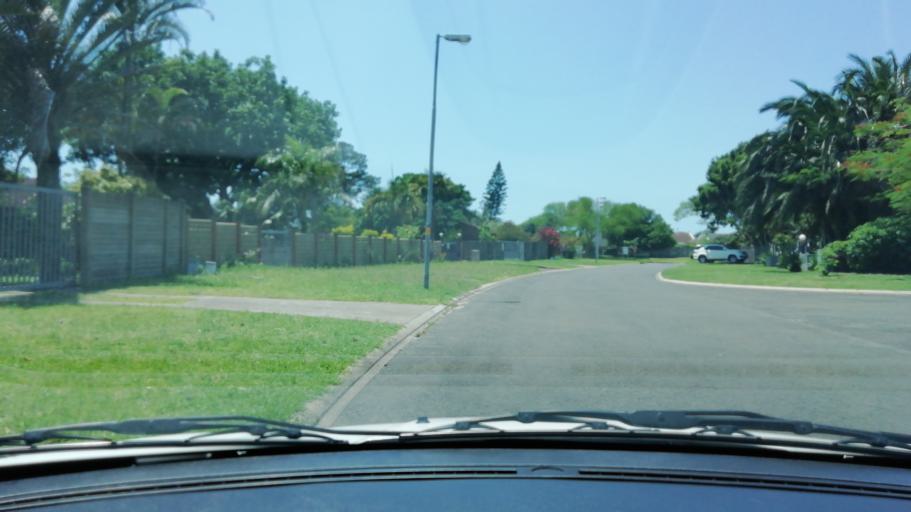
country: ZA
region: KwaZulu-Natal
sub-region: uThungulu District Municipality
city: Richards Bay
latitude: -28.7360
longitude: 32.0473
